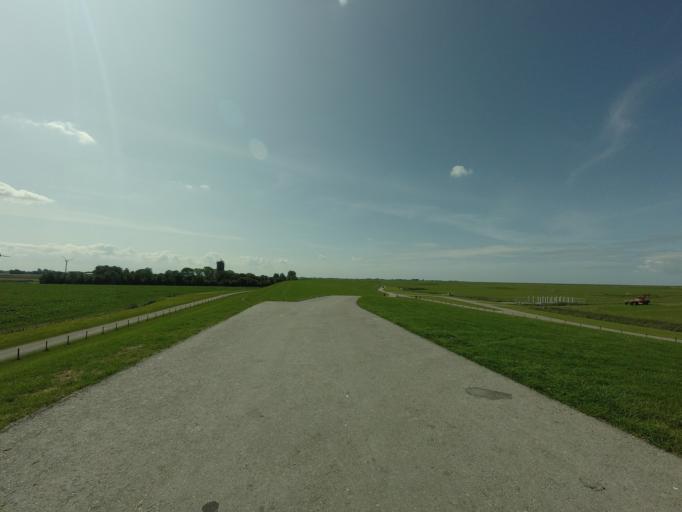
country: NL
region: Friesland
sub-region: Gemeente Ferwerderadiel
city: Hallum
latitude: 53.3312
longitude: 5.7755
